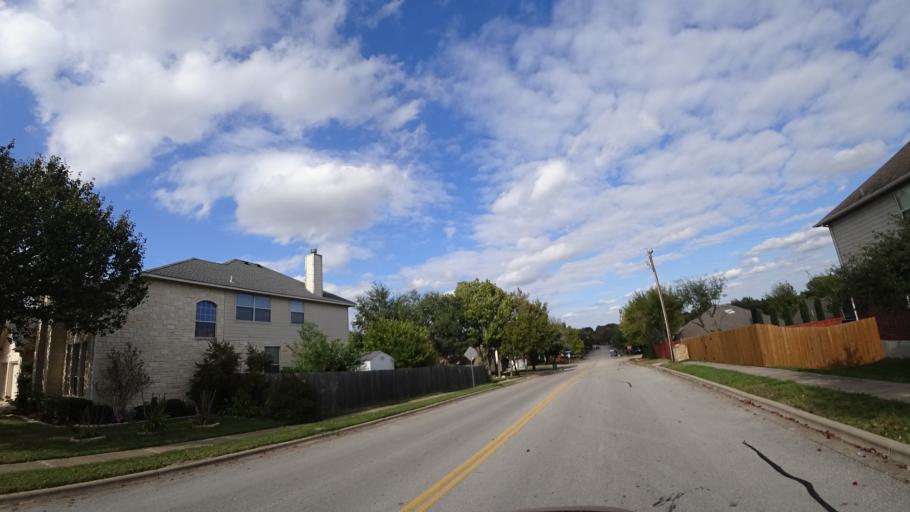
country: US
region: Texas
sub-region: Travis County
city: Pflugerville
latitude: 30.4312
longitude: -97.6284
